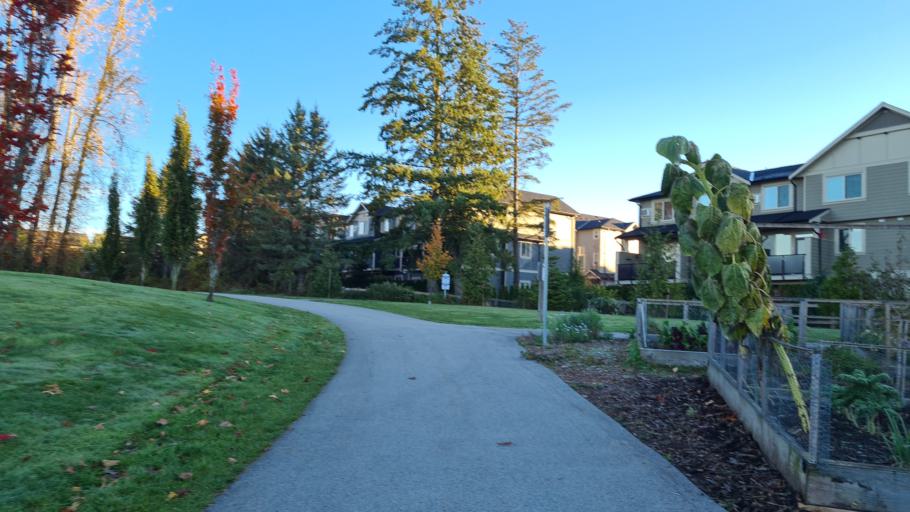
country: CA
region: British Columbia
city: Langley
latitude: 49.1304
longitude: -122.6707
